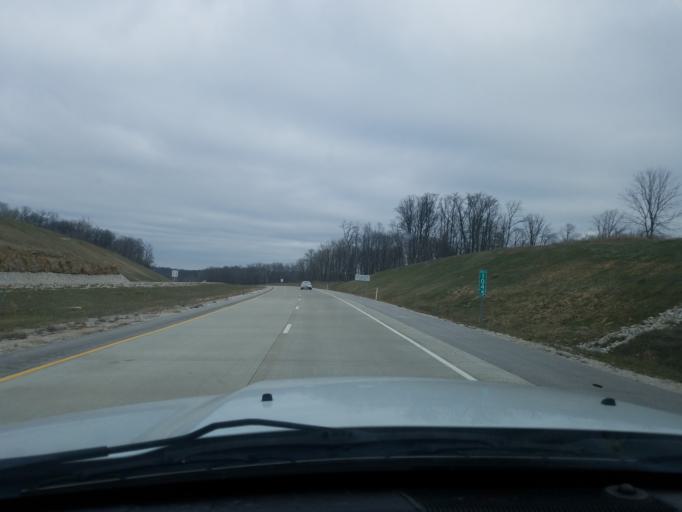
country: US
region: Indiana
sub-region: Monroe County
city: Bloomington
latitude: 39.0426
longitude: -86.6805
